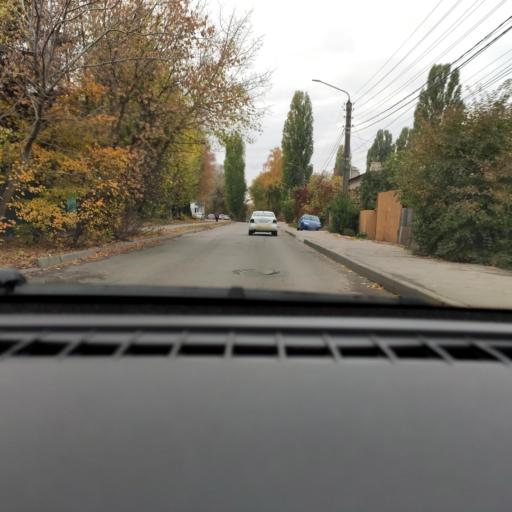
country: RU
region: Voronezj
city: Voronezh
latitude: 51.6925
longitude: 39.1699
